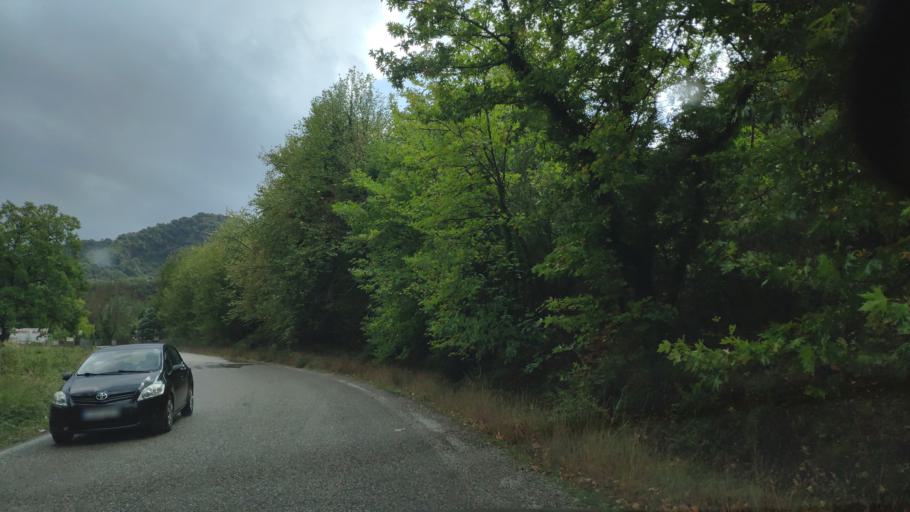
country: GR
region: West Greece
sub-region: Nomos Aitolias kai Akarnanias
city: Krikellos
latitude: 38.9649
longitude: 21.3283
